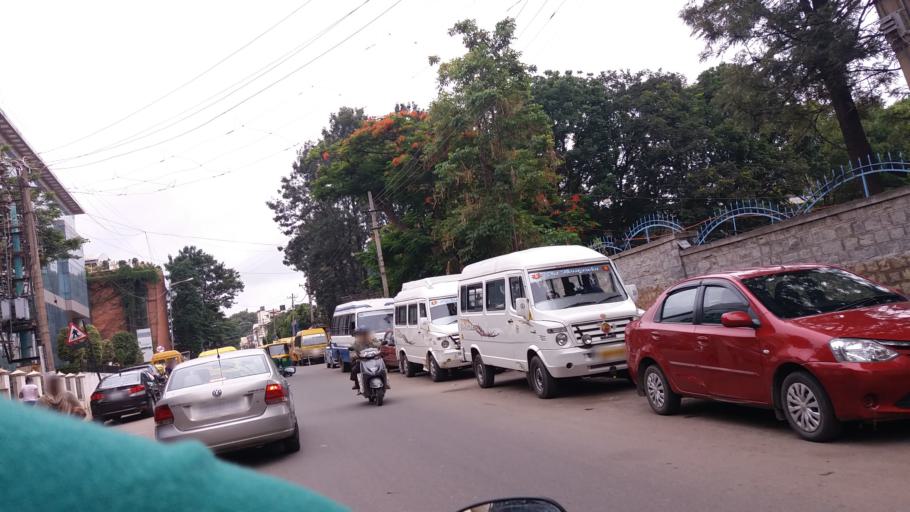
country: IN
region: Karnataka
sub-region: Bangalore Urban
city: Bangalore
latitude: 12.9699
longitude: 77.6286
